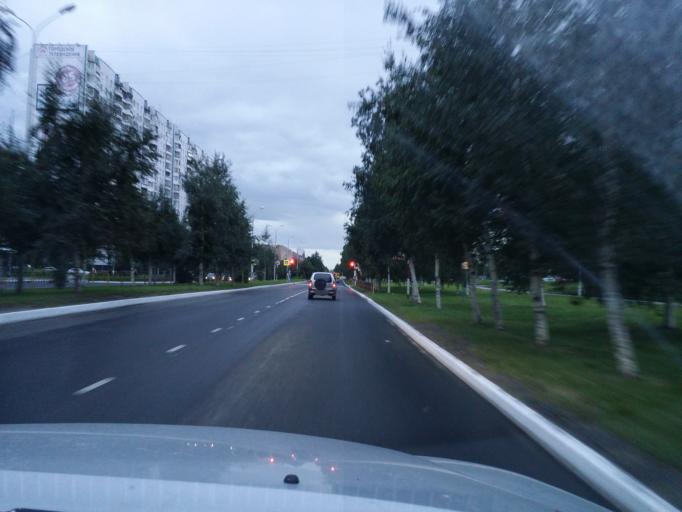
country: RU
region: Khanty-Mansiyskiy Avtonomnyy Okrug
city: Nizhnevartovsk
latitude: 60.9378
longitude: 76.5936
